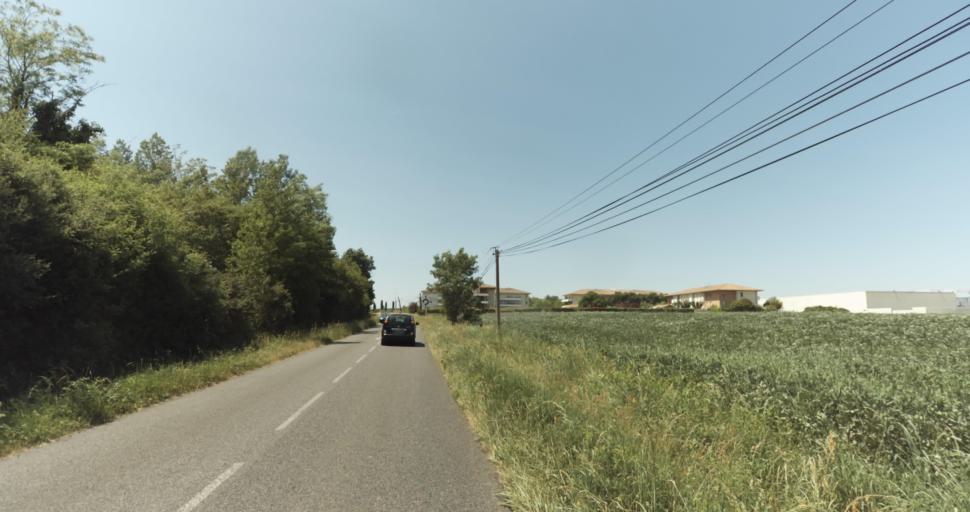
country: FR
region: Midi-Pyrenees
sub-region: Departement de la Haute-Garonne
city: La Salvetat-Saint-Gilles
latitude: 43.5991
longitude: 1.2654
